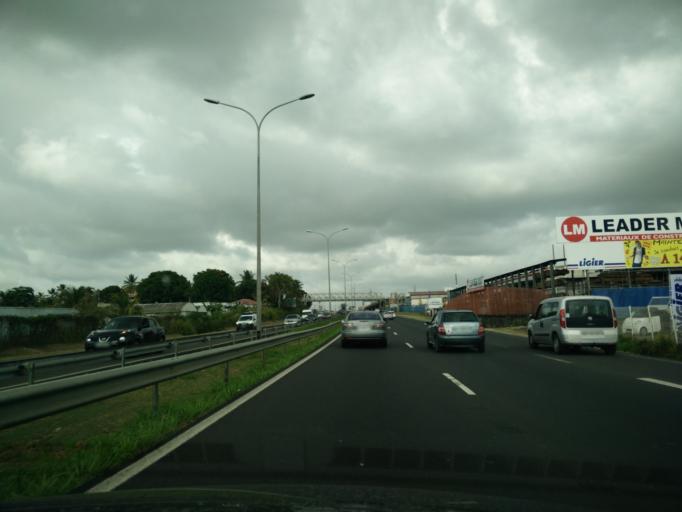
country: GP
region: Guadeloupe
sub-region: Guadeloupe
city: Pointe-a-Pitre
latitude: 16.2541
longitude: -61.5609
